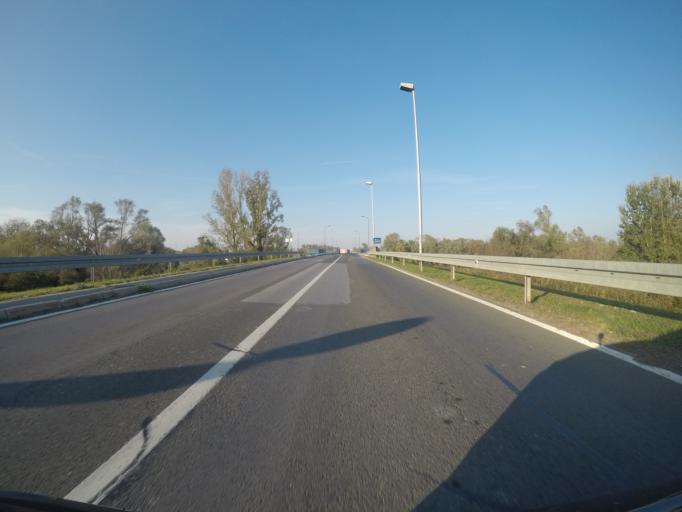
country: HU
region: Somogy
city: Barcs
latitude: 45.9440
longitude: 17.4613
